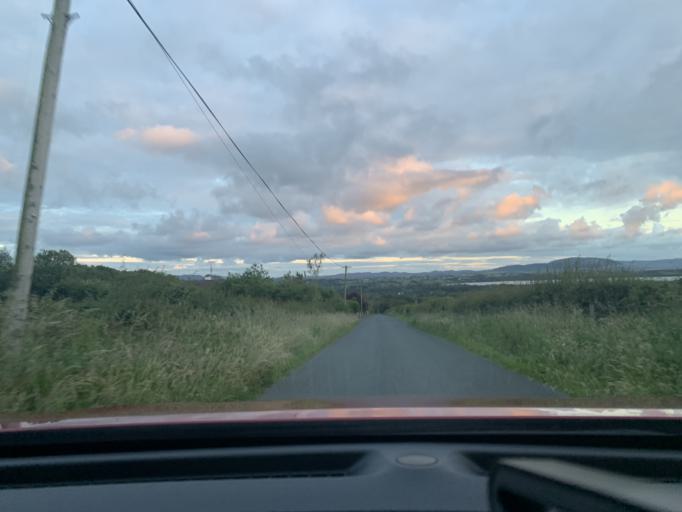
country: IE
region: Connaught
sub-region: Sligo
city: Sligo
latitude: 54.3513
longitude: -8.4884
